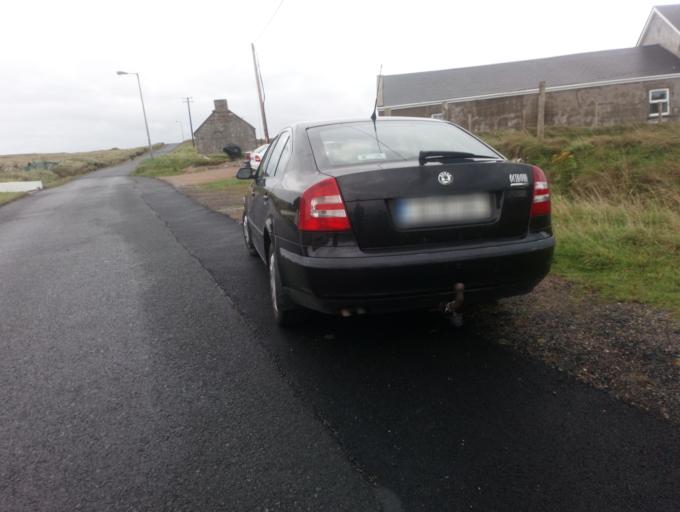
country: IE
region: Ulster
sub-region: County Donegal
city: Derrybeg
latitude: 55.2638
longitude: -8.2217
